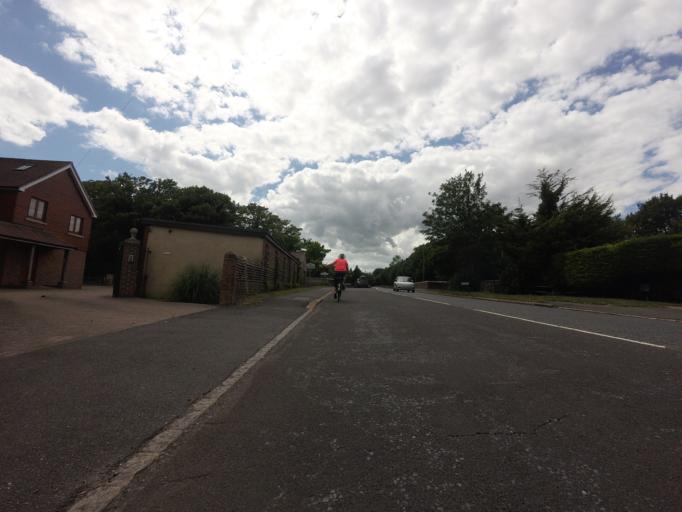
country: GB
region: England
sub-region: East Sussex
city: Pevensey
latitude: 50.8210
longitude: 0.3406
